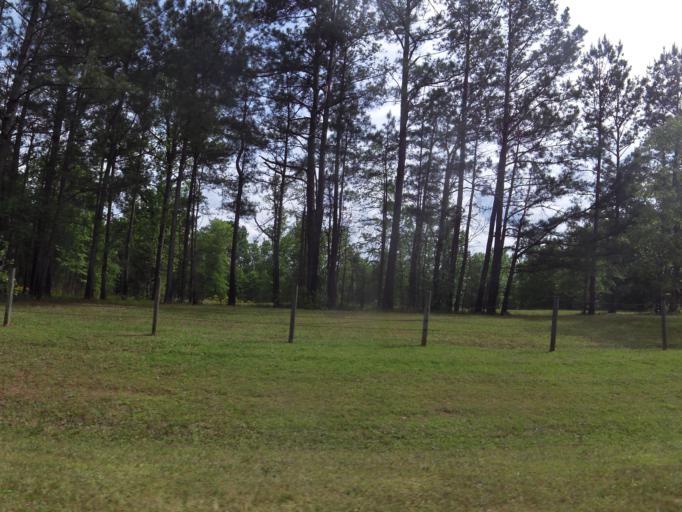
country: US
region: Georgia
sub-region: McDuffie County
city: Thomson
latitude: 33.5346
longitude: -82.4918
